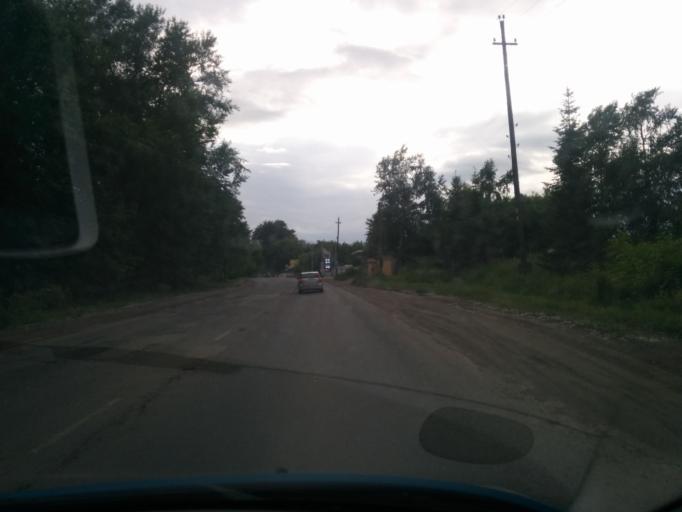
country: RU
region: Perm
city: Perm
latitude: 58.0032
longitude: 56.1861
